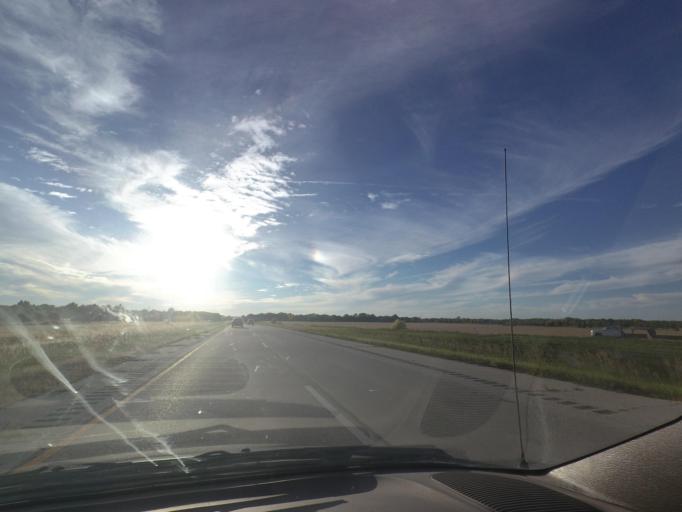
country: US
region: Illinois
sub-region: Sangamon County
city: Jerome
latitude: 39.7522
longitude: -89.7523
